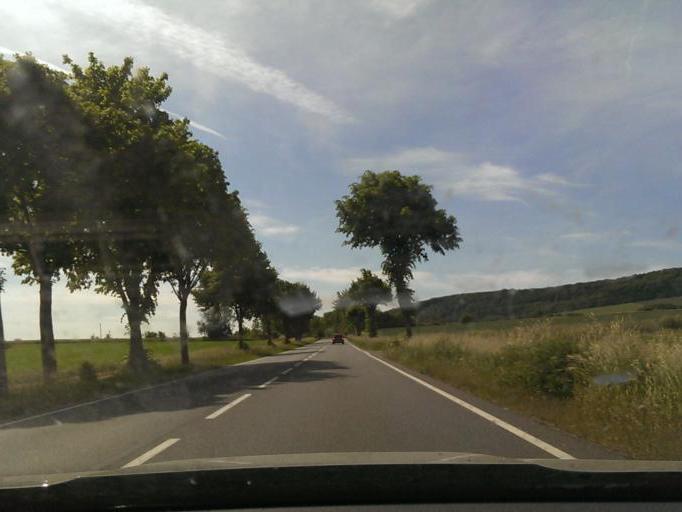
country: DE
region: Lower Saxony
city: Banteln
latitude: 52.0522
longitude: 9.7545
